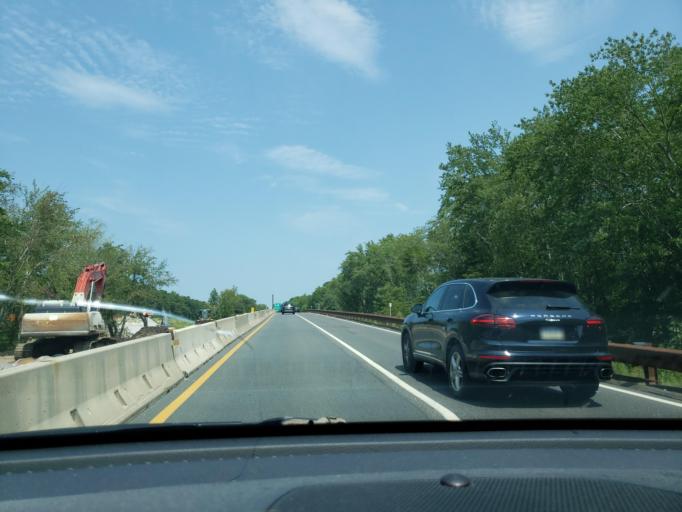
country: US
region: New Jersey
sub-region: Atlantic County
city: Northfield
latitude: 39.3783
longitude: -74.5795
